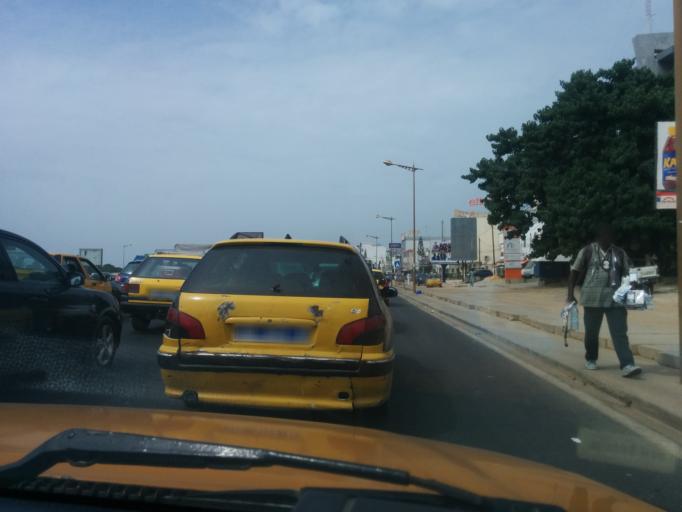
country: SN
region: Dakar
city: Mermoz Boabab
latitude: 14.7257
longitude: -17.4713
